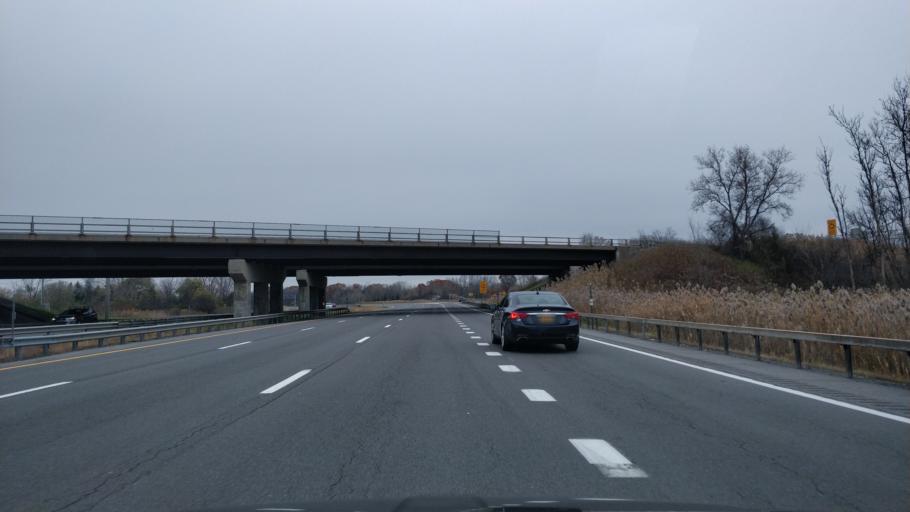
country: US
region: New York
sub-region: Onondaga County
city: North Syracuse
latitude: 43.1407
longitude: -76.1133
